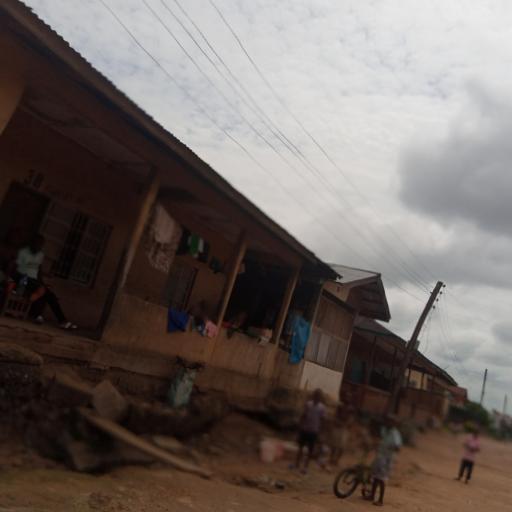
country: SL
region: Eastern Province
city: Kenema
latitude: 7.8889
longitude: -11.1890
